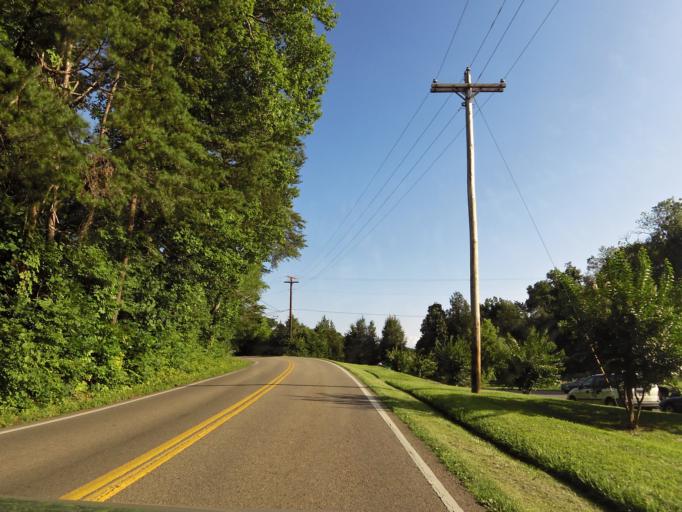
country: US
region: Tennessee
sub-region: Blount County
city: Maryville
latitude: 35.7087
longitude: -83.9689
